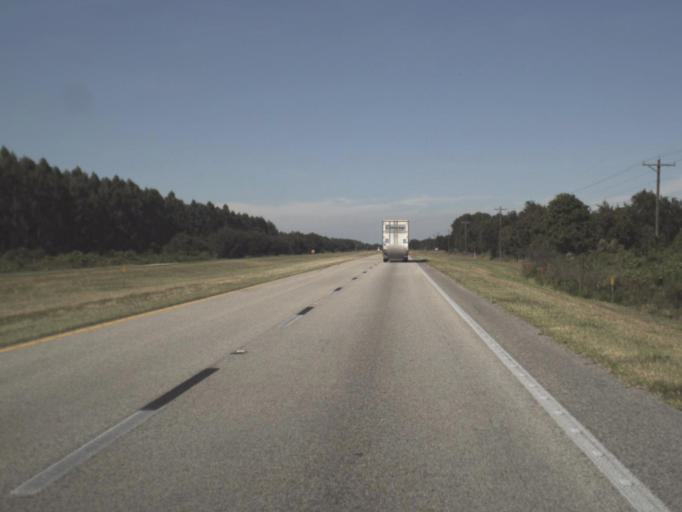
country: US
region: Florida
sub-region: Hendry County
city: Port LaBelle
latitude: 26.9948
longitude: -81.3271
